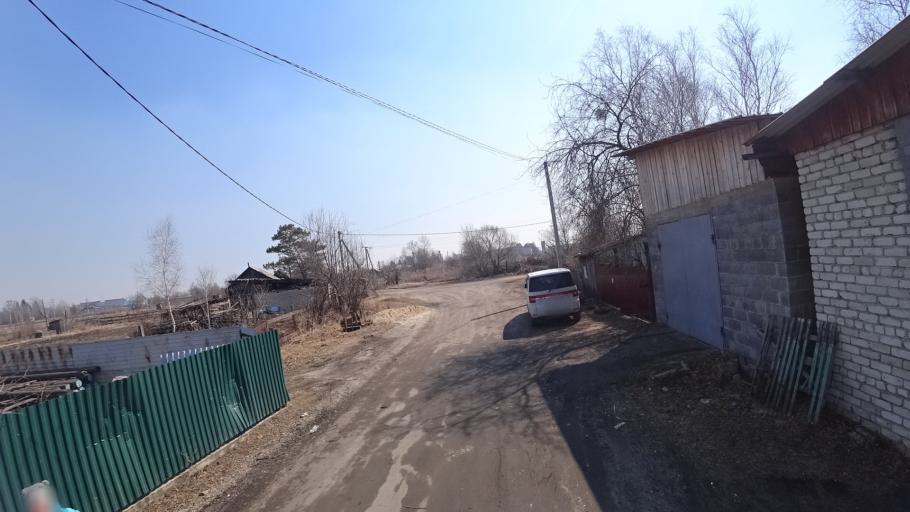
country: RU
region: Amur
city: Novobureyskiy
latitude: 49.7887
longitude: 129.8419
